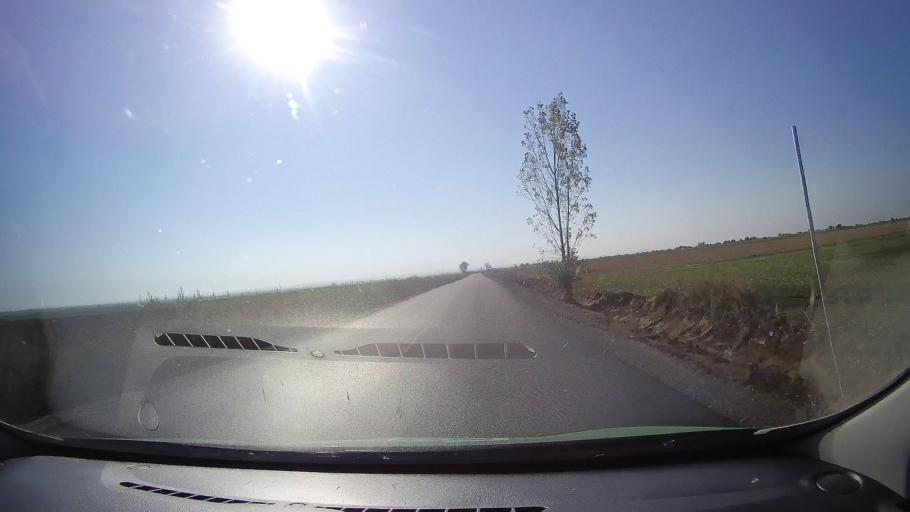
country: RO
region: Satu Mare
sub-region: Comuna Tiream
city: Tiream
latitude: 47.6371
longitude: 22.4662
